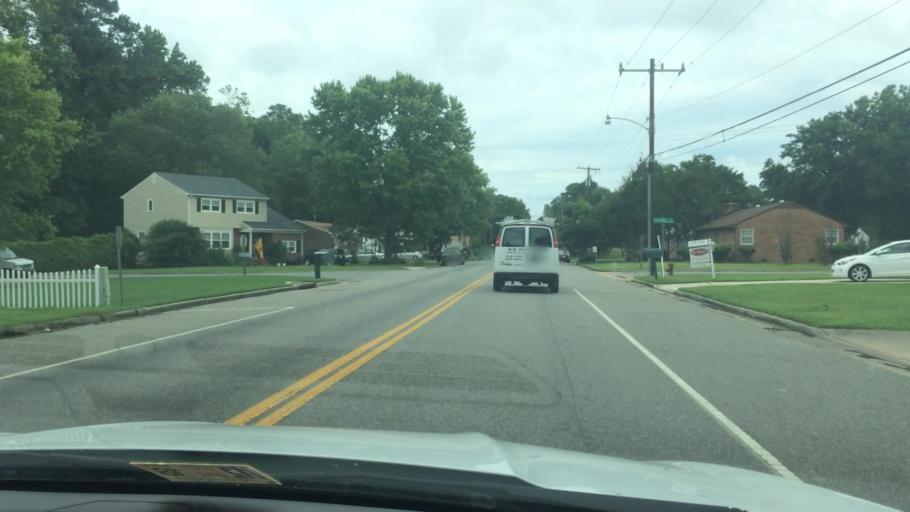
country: US
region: Virginia
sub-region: City of Williamsburg
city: Williamsburg
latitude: 37.2737
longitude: -76.6722
